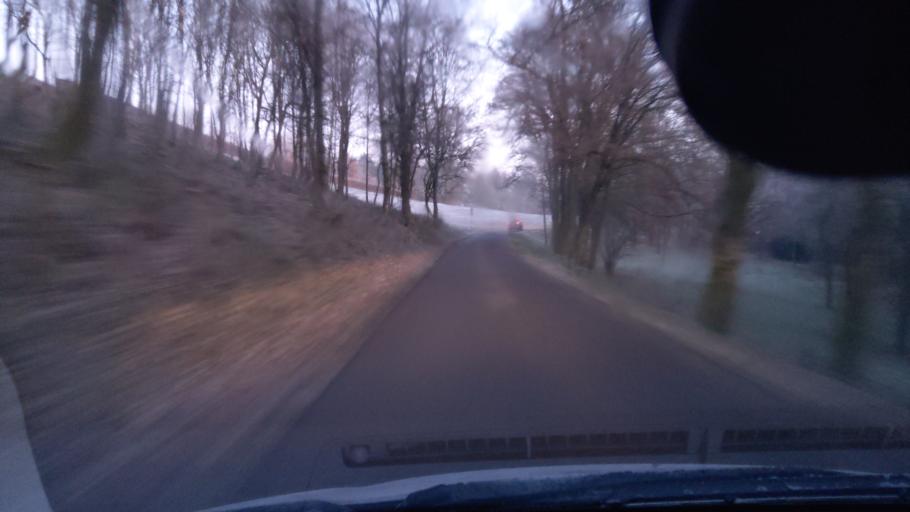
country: DE
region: Saarland
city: Tholey
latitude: 49.5127
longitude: 7.0155
